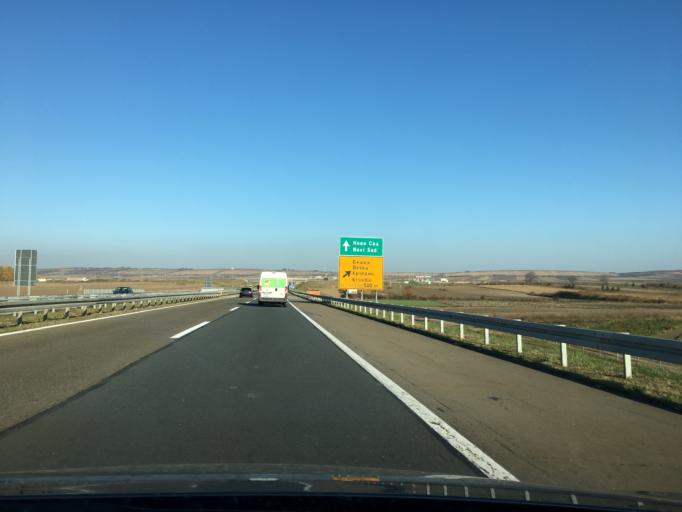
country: RS
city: Beska
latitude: 45.1284
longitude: 20.0913
